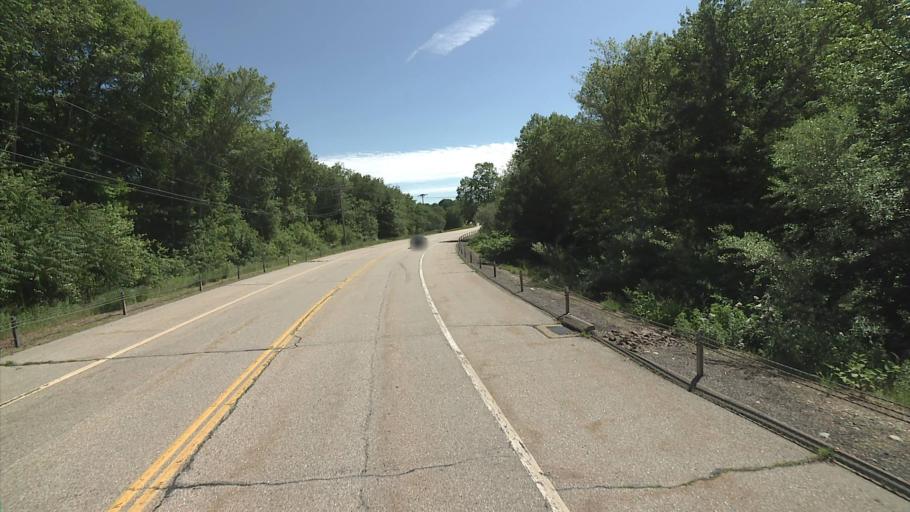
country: US
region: Connecticut
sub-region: New London County
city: Pawcatuck
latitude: 41.4177
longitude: -71.8525
